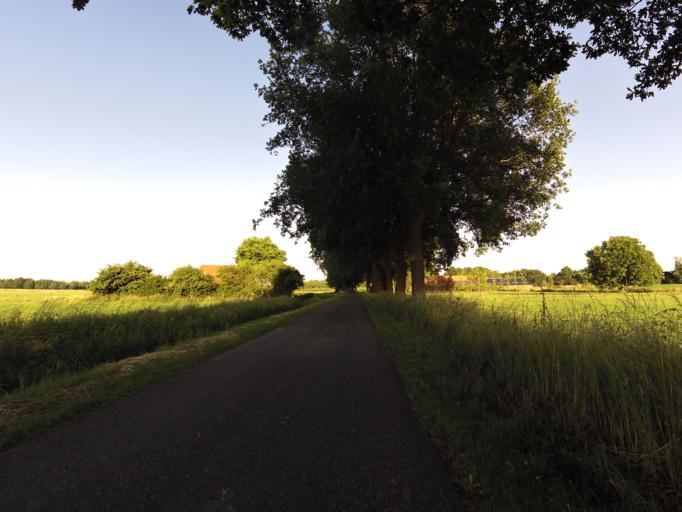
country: DE
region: North Rhine-Westphalia
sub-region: Regierungsbezirk Munster
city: Isselburg
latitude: 51.8695
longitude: 6.4361
